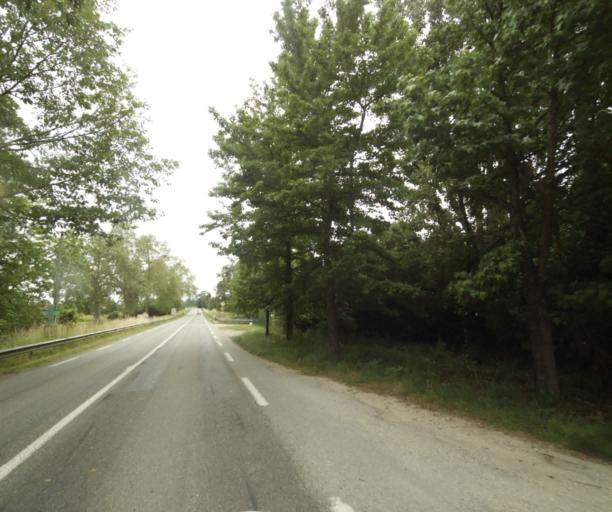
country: FR
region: Midi-Pyrenees
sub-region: Departement du Tarn-et-Garonne
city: Saint-Nauphary
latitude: 43.9701
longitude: 1.4217
